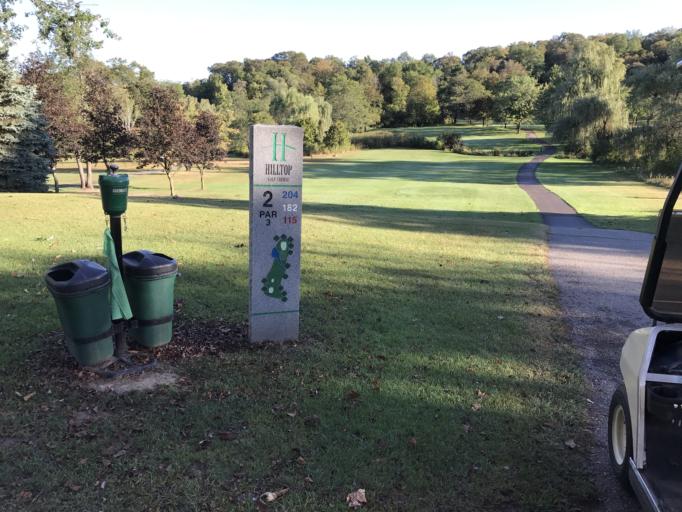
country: US
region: Michigan
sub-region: Wayne County
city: Plymouth
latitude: 42.3697
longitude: -83.5065
